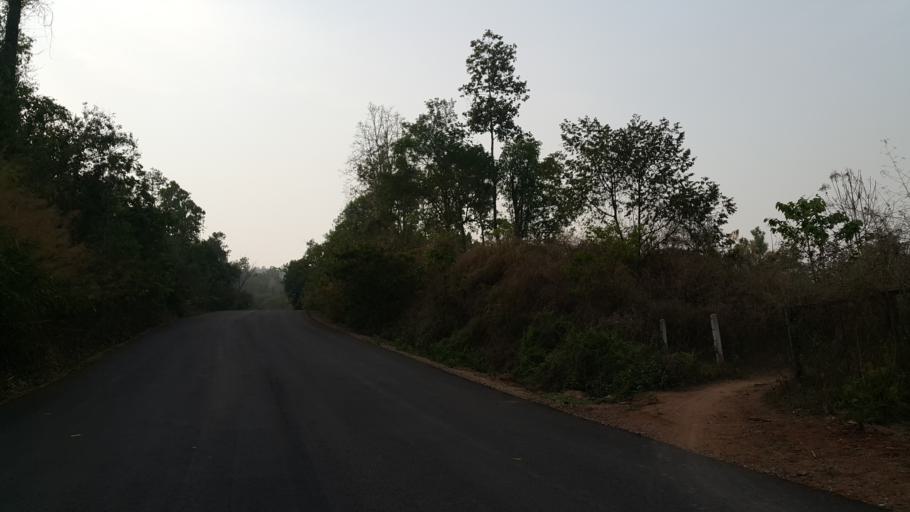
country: TH
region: Chiang Mai
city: Mae On
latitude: 18.7510
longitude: 99.3011
